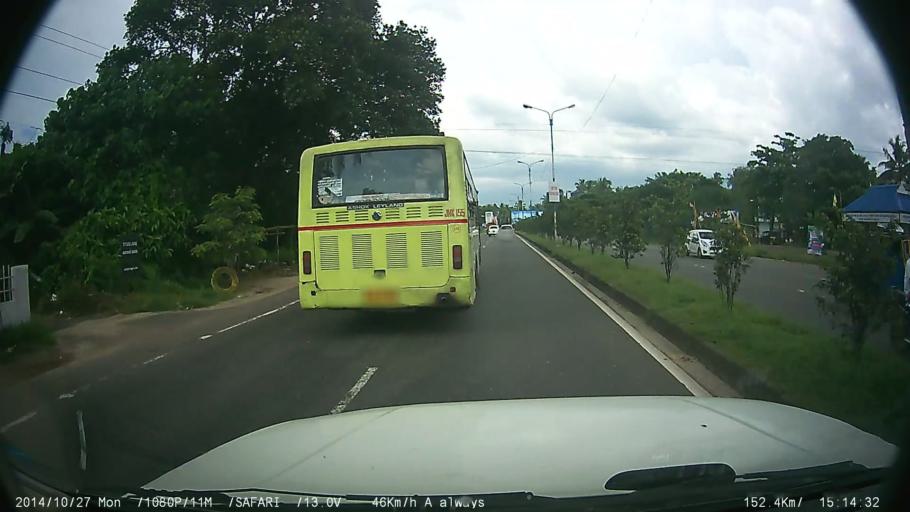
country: IN
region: Kerala
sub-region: Ernakulam
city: Aluva
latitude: 10.1461
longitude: 76.3533
